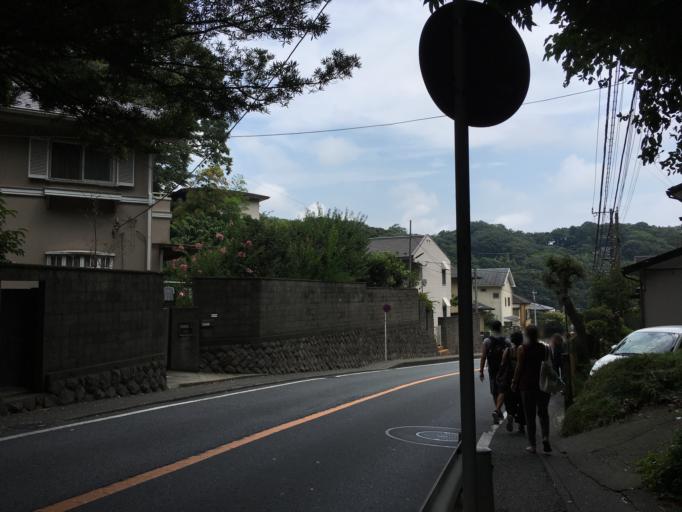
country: JP
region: Kanagawa
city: Kamakura
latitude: 35.3290
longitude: 139.5543
